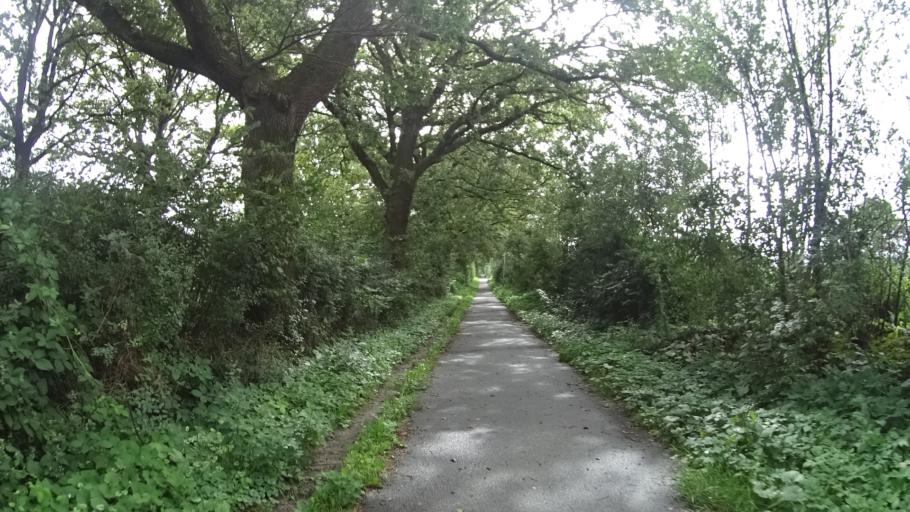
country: DE
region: Schleswig-Holstein
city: Tangstedt
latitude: 53.7413
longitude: 10.0704
